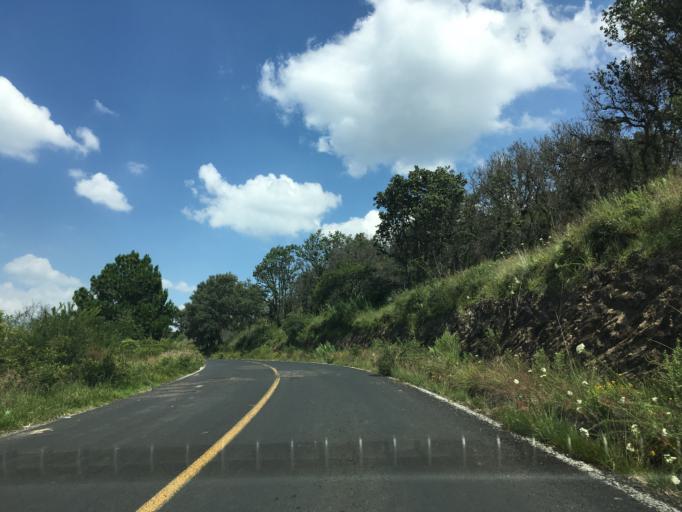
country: MX
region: Michoacan
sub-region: Morelia
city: Montana Monarca (Punta Altozano)
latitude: 19.6422
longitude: -101.2001
